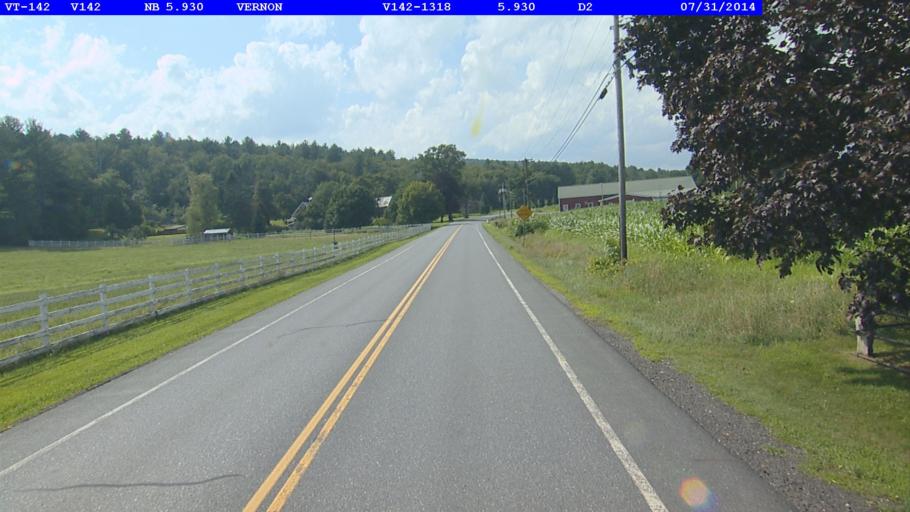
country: US
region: New Hampshire
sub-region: Cheshire County
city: Hinsdale
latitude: 42.7879
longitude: -72.5308
